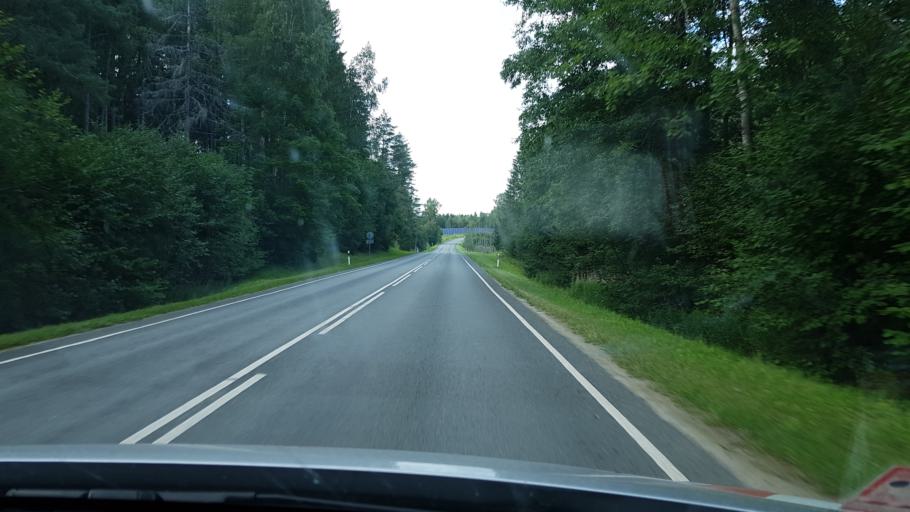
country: EE
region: Vorumaa
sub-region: Antsla vald
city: Vana-Antsla
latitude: 57.9745
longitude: 26.4652
